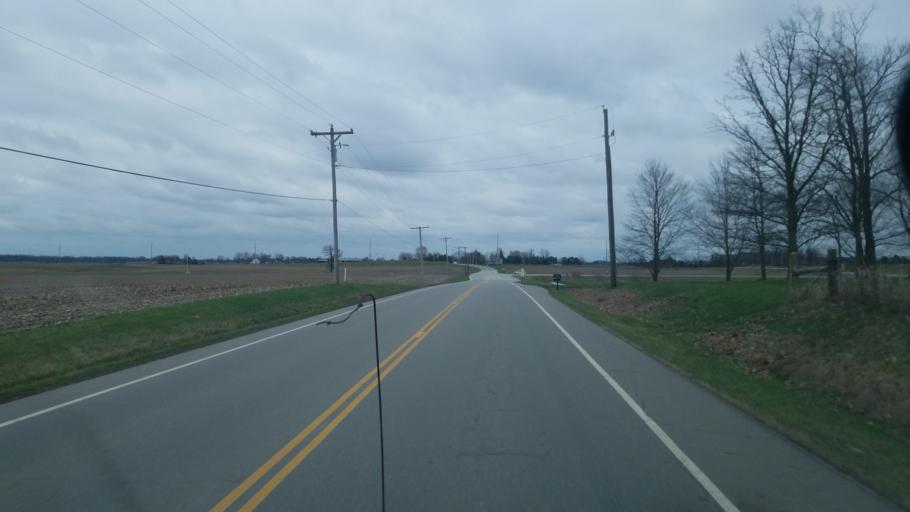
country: US
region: Ohio
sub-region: Fayette County
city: Washington Court House
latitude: 39.5531
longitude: -83.4882
